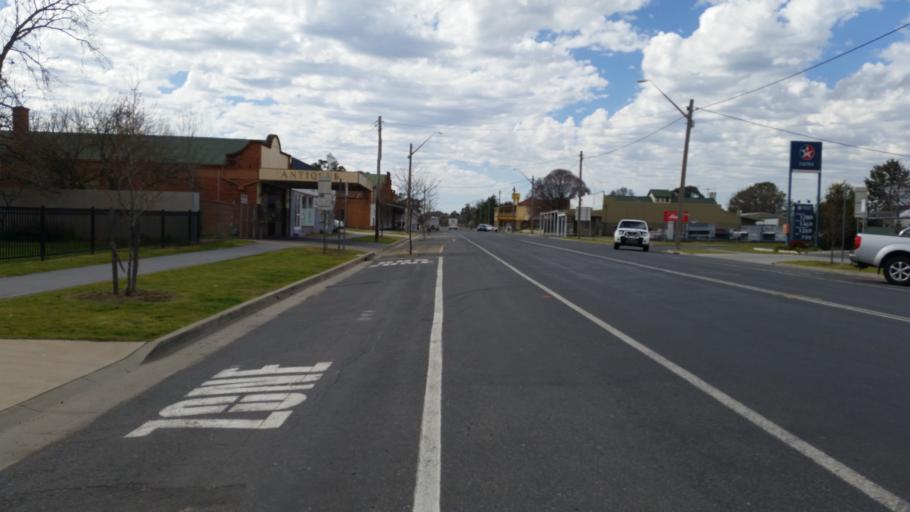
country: AU
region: New South Wales
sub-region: Greater Hume Shire
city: Holbrook
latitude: -35.7210
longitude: 147.3159
